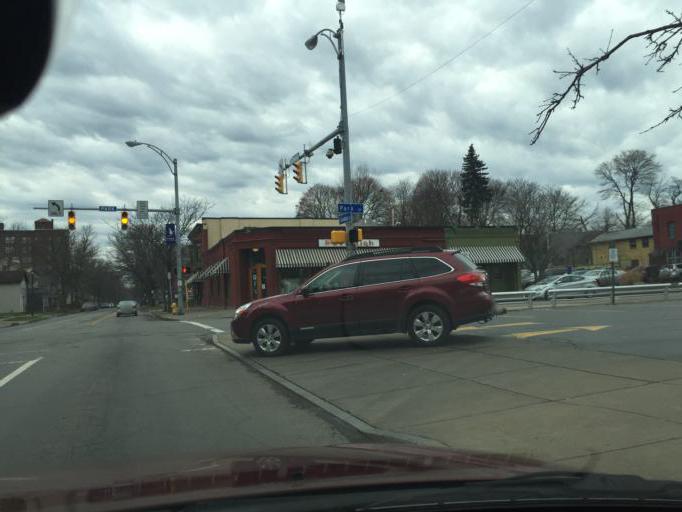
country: US
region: New York
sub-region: Monroe County
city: Rochester
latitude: 43.1507
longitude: -77.5897
